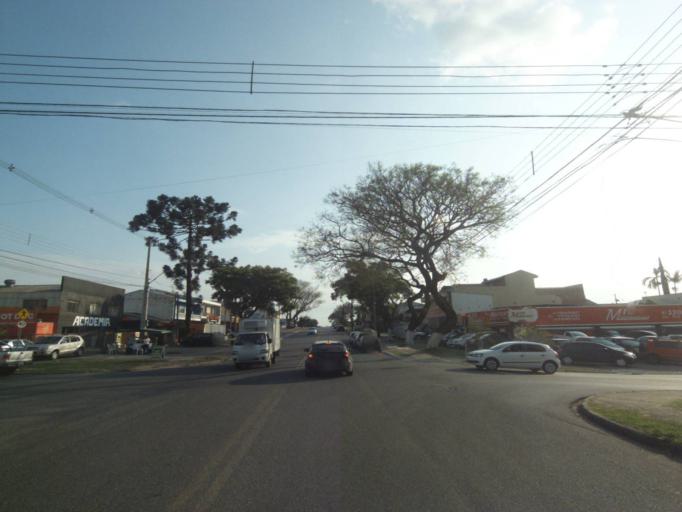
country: BR
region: Parana
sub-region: Curitiba
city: Curitiba
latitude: -25.4840
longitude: -49.3271
